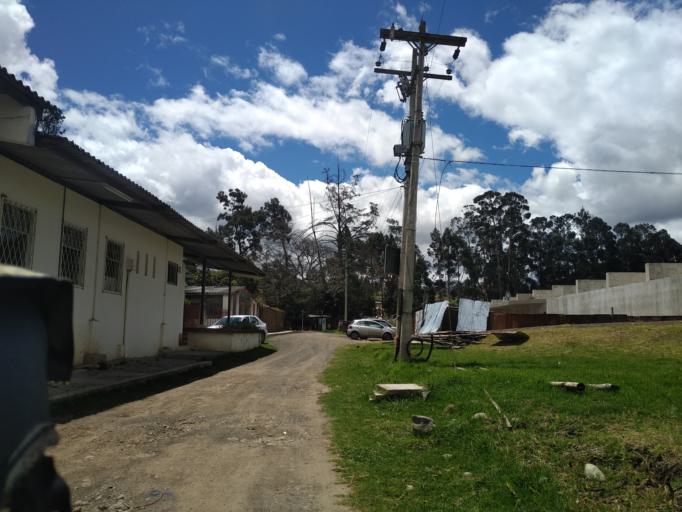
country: EC
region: Azuay
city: Cuenca
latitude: -2.8921
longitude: -79.0360
